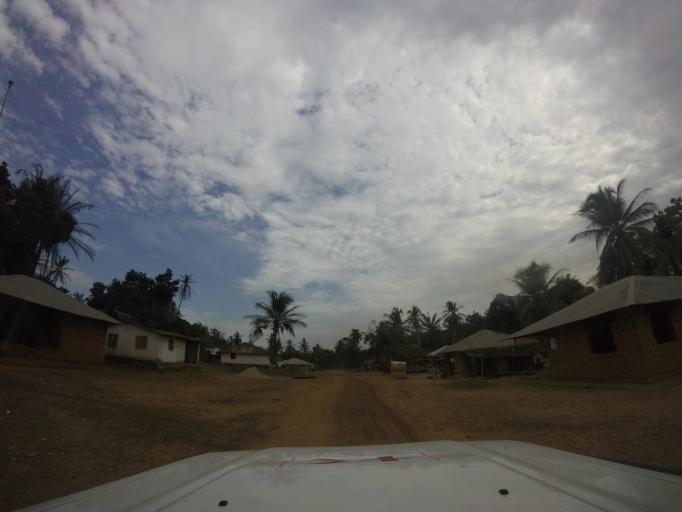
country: LR
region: Grand Cape Mount
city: Robertsport
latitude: 7.0194
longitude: -11.2884
